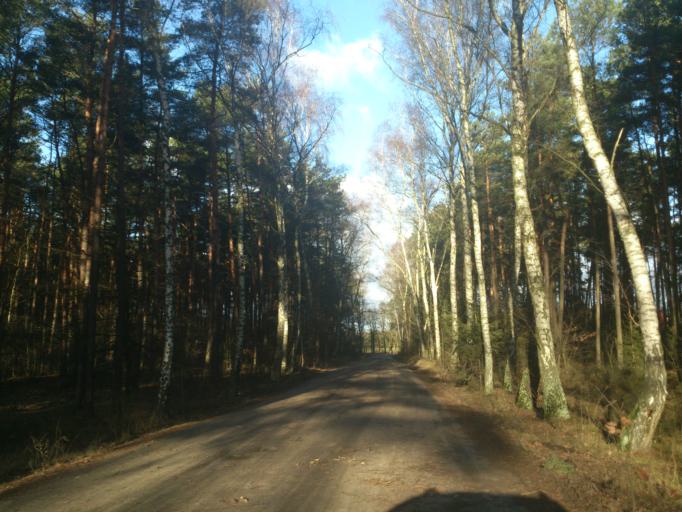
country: PL
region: Kujawsko-Pomorskie
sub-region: Powiat torunski
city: Lubicz Gorny
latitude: 53.0127
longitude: 18.7983
